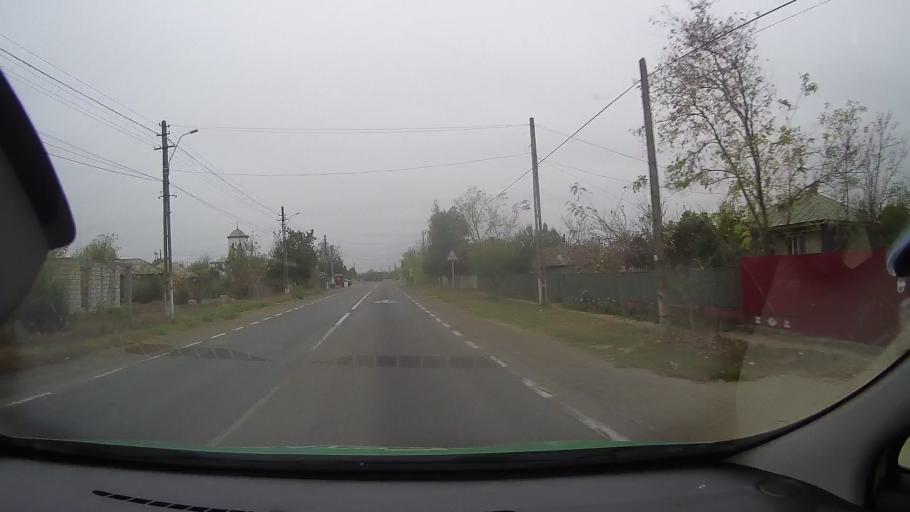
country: RO
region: Braila
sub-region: Comuna Baraganul
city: Baraganul
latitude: 44.8046
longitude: 27.5133
